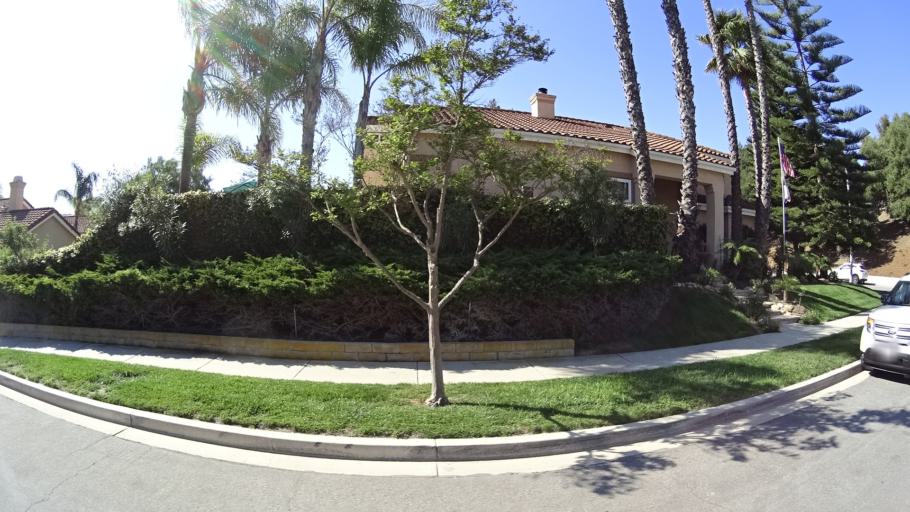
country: US
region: California
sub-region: Ventura County
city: Simi Valley
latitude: 34.2483
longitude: -118.8209
